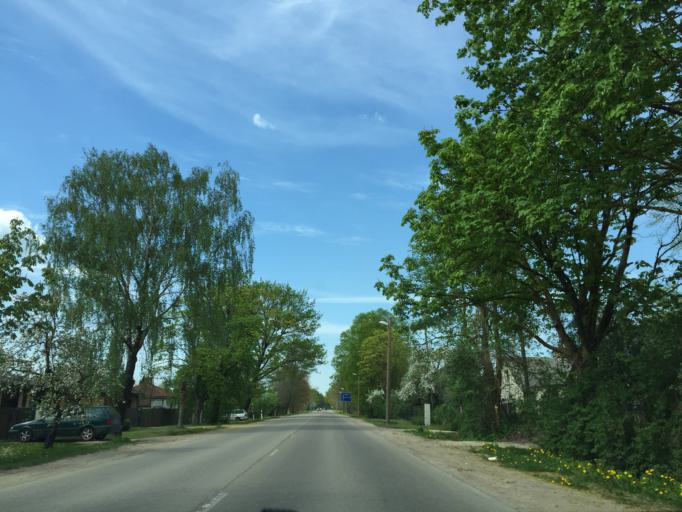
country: LV
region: Jelgava
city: Jelgava
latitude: 56.6667
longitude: 23.7332
